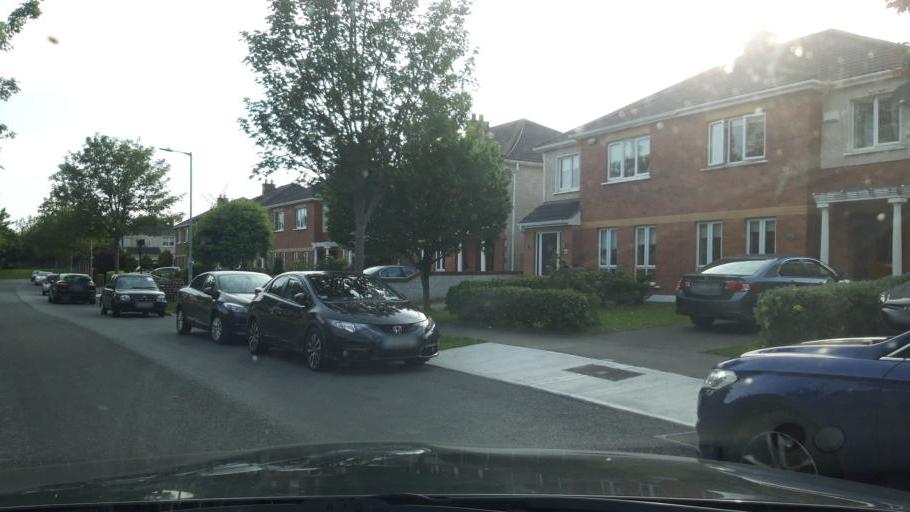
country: IE
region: Leinster
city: Hartstown
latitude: 53.4016
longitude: -6.4326
